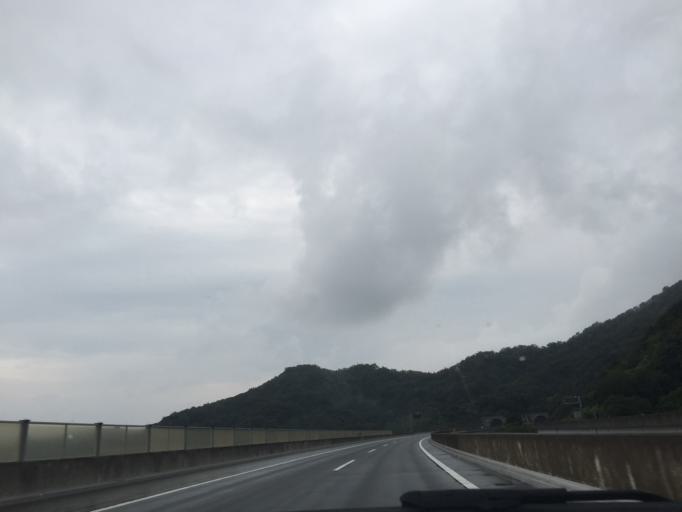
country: JP
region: Tokushima
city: Narutocho-mitsuishi
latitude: 34.2022
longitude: 134.6212
